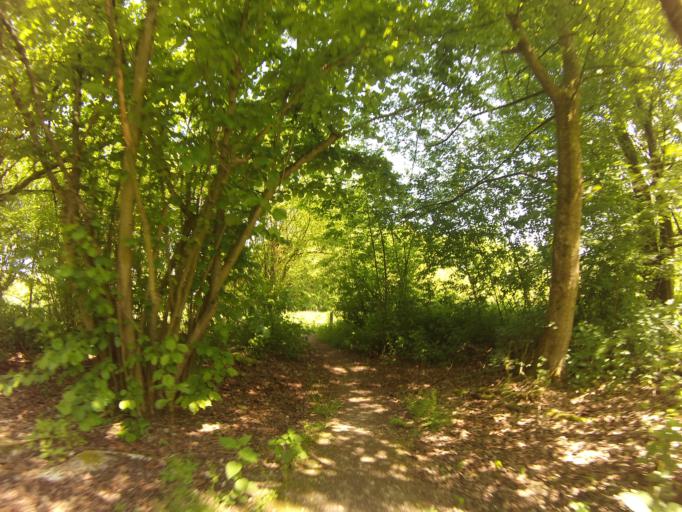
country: NL
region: Flevoland
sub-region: Gemeente Zeewolde
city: Zeewolde
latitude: 52.2992
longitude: 5.5230
